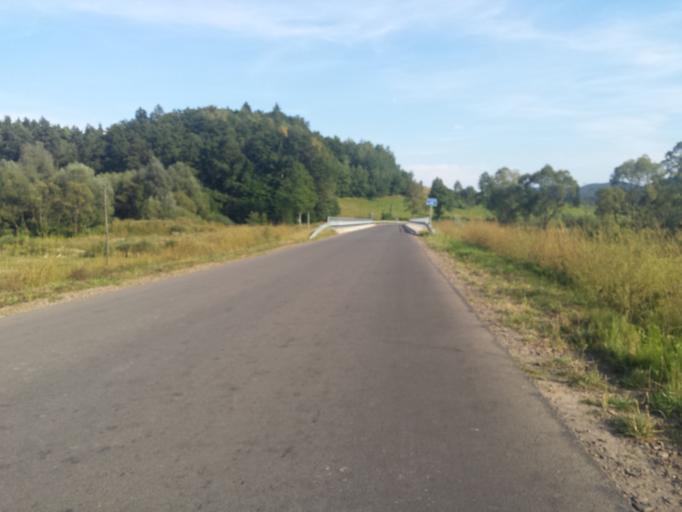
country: PL
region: Subcarpathian Voivodeship
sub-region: Powiat leski
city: Uherce Mineralne
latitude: 49.4511
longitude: 22.3906
